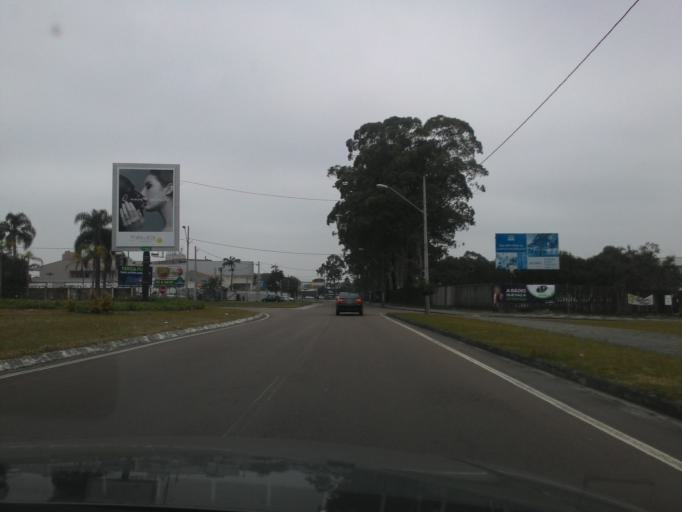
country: BR
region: Parana
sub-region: Pinhais
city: Pinhais
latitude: -25.4485
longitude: -49.2301
